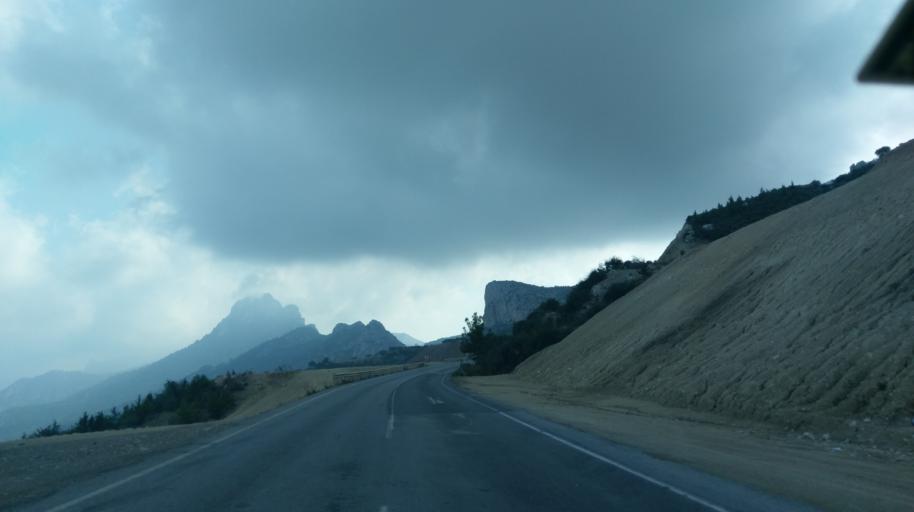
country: CY
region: Keryneia
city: Kyrenia
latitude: 35.2954
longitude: 33.4402
